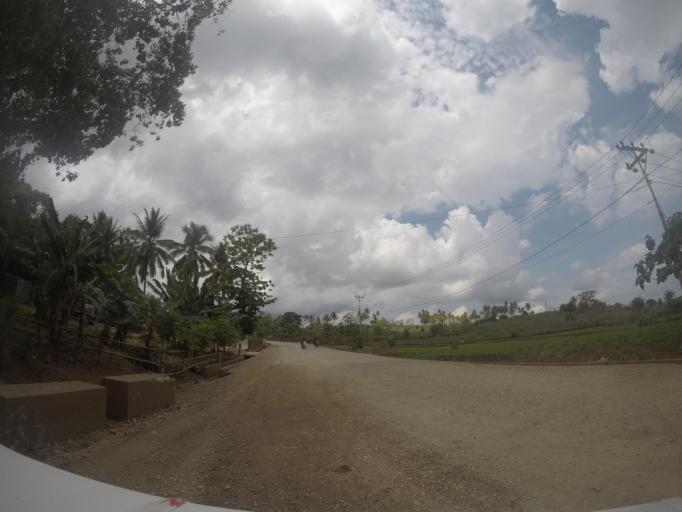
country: TL
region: Baucau
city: Baucau
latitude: -8.5346
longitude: 126.4208
